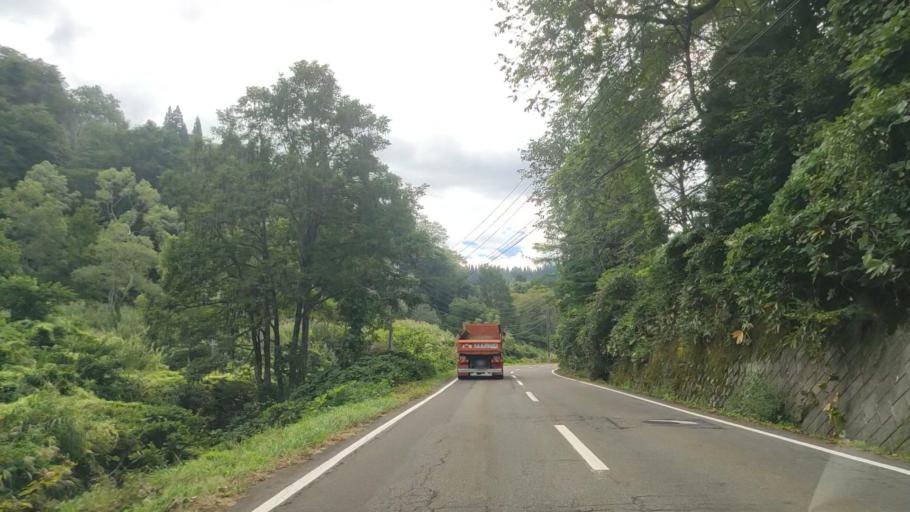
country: JP
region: Nagano
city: Iiyama
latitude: 36.8845
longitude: 138.3212
